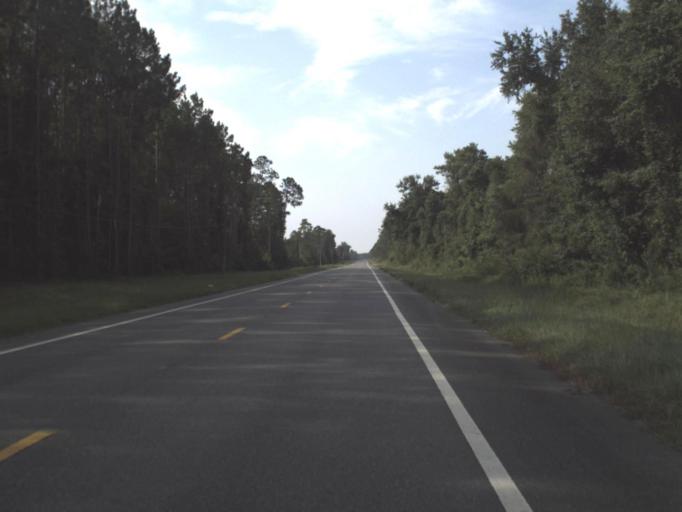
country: US
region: Florida
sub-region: Taylor County
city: Perry
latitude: 30.2411
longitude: -83.6200
